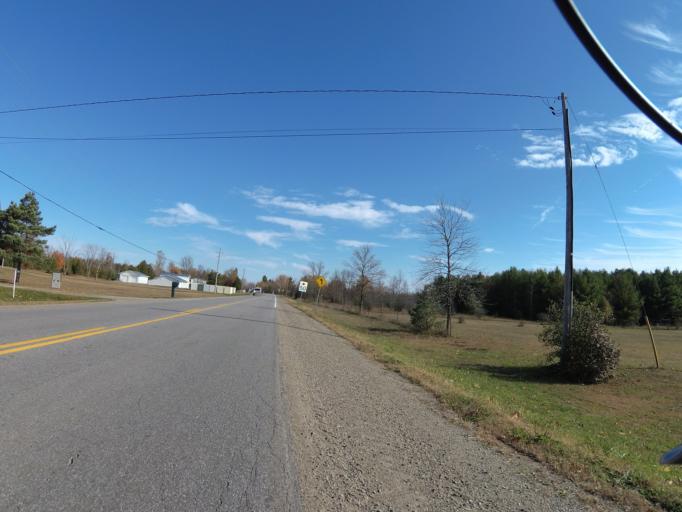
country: CA
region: Ontario
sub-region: Lanark County
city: Smiths Falls
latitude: 44.8383
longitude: -75.9416
